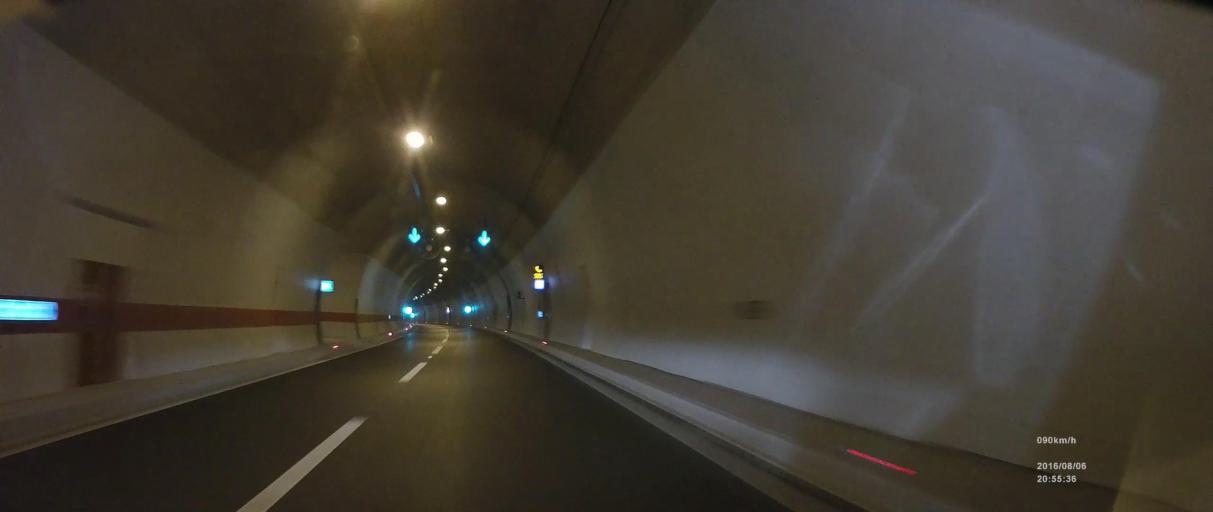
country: BA
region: Federation of Bosnia and Herzegovina
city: Vitina
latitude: 43.1626
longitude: 17.4689
